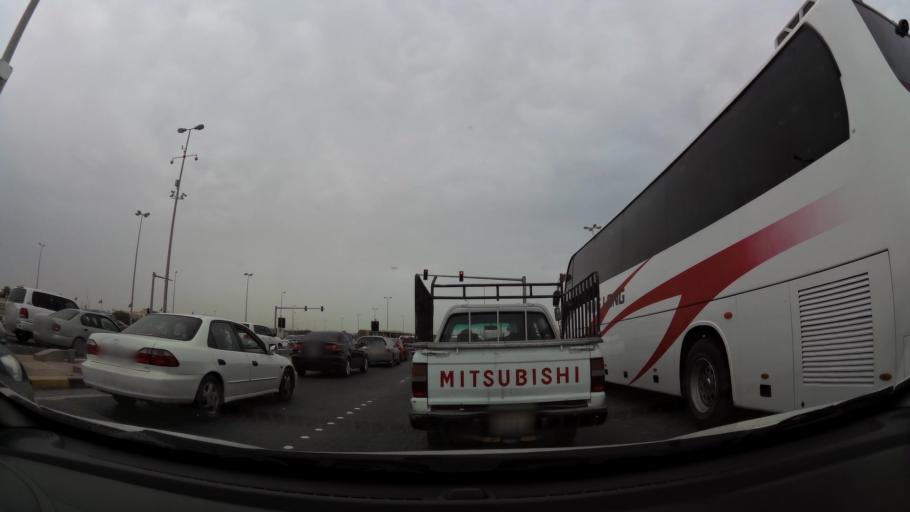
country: BH
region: Northern
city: Madinat `Isa
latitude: 26.1579
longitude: 50.5365
